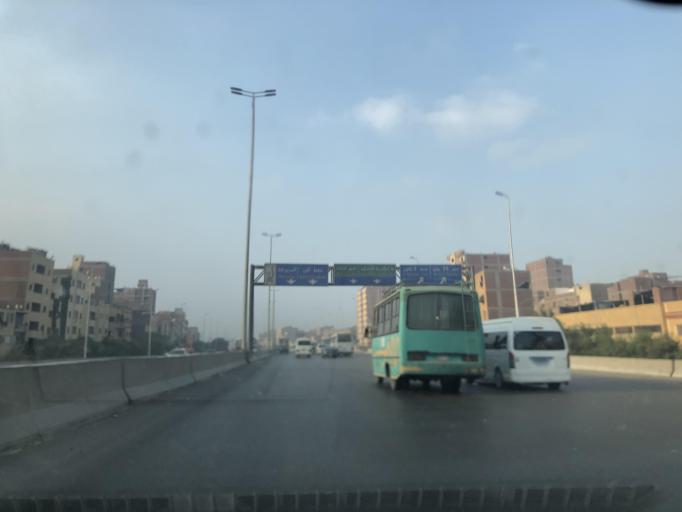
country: EG
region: Al Jizah
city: Awsim
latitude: 30.0706
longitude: 31.1753
